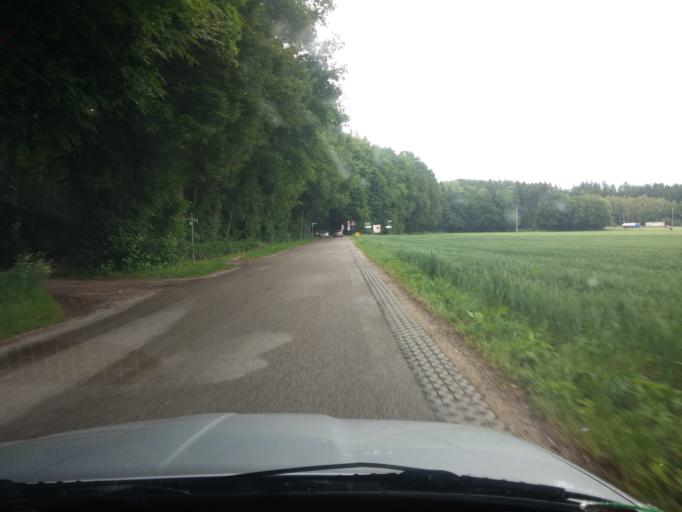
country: DE
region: Bavaria
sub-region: Swabia
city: Illertissen
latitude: 48.2309
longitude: 10.1196
